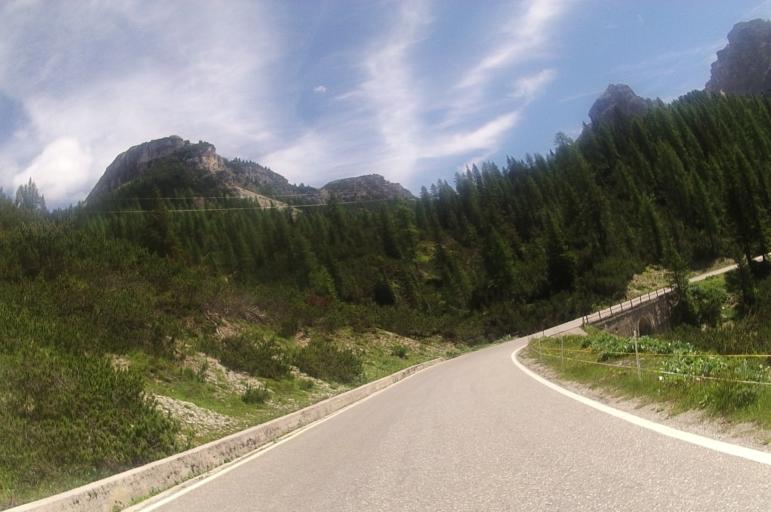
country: IT
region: Trentino-Alto Adige
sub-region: Bolzano
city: Sesto
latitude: 46.6065
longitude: 12.2734
